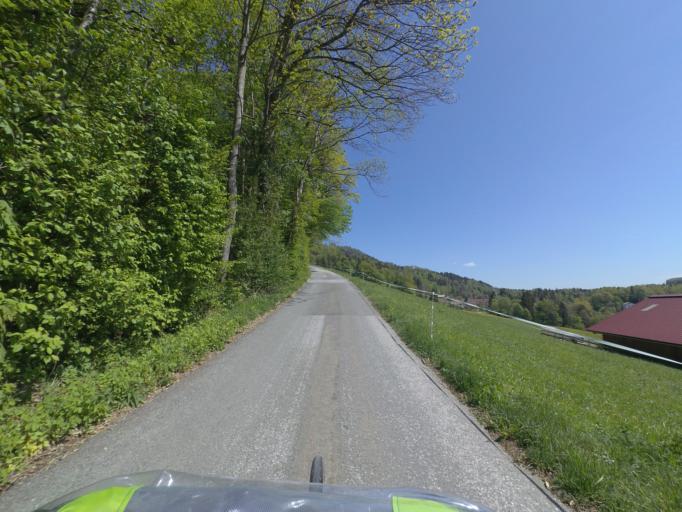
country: AT
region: Salzburg
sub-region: Politischer Bezirk Salzburg-Umgebung
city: Hallwang
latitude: 47.8209
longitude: 13.0941
